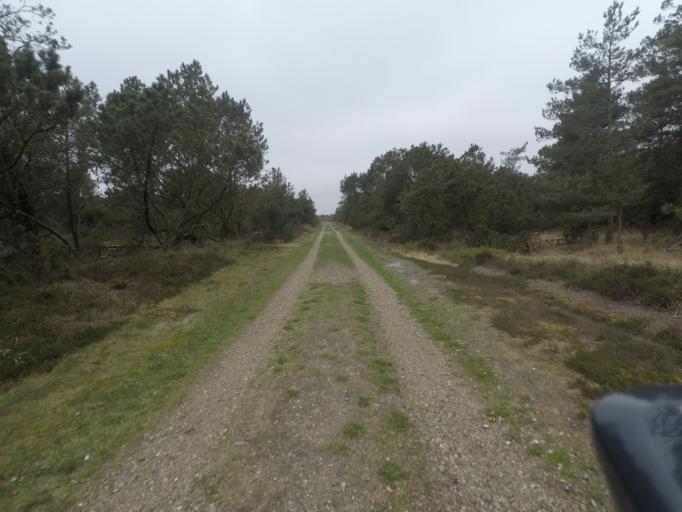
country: DE
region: Schleswig-Holstein
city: List
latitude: 55.1238
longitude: 8.5303
